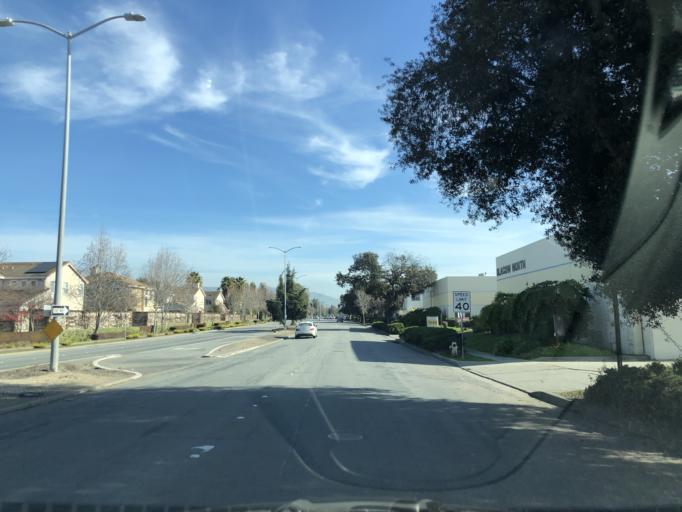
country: US
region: California
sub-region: Alameda County
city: Newark
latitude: 37.5460
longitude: -122.0174
